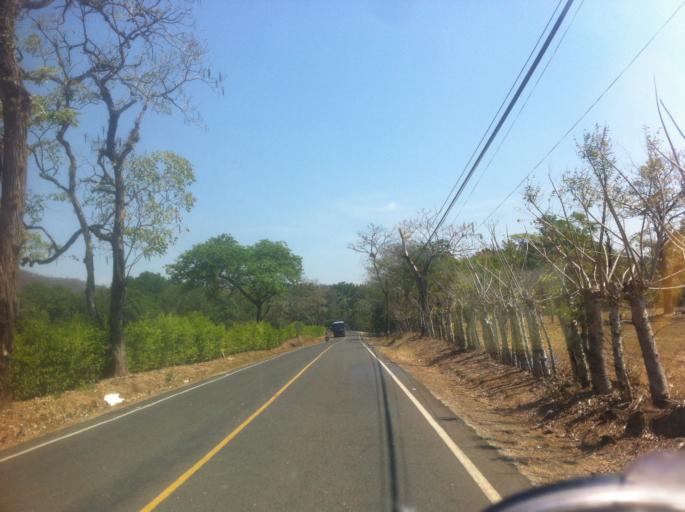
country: CR
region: Guanacaste
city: Hojancha
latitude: 10.0938
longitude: -85.4610
